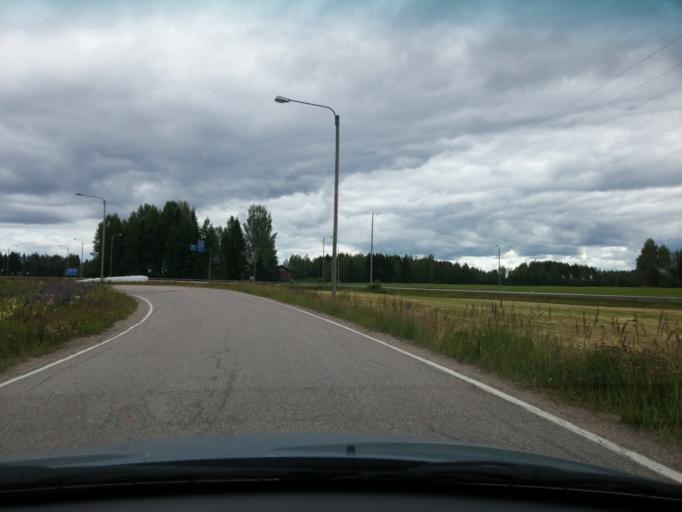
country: FI
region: Central Finland
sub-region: AEaenekoski
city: AEaenekoski
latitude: 62.7442
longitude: 25.7707
